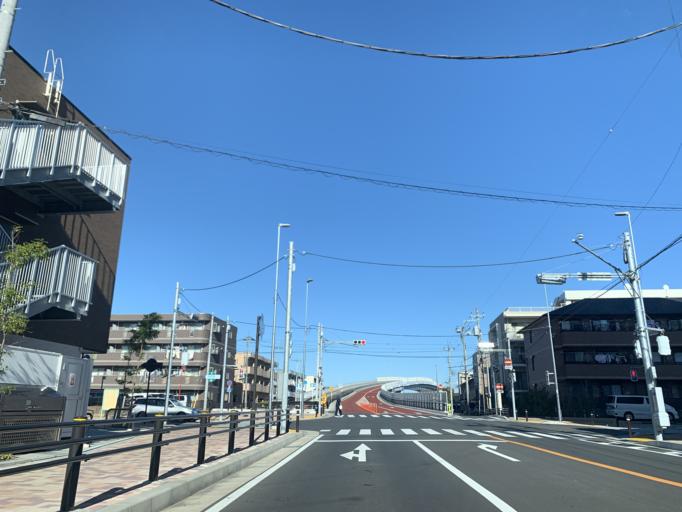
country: JP
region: Tokyo
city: Urayasu
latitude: 35.6887
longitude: 139.9317
